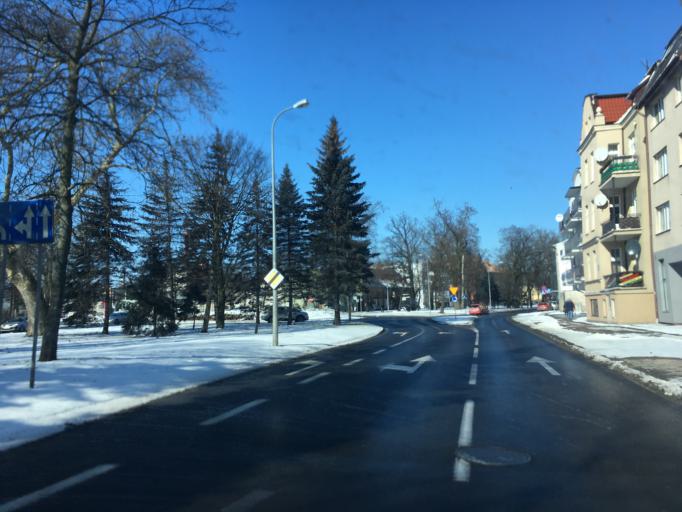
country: PL
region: Pomeranian Voivodeship
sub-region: Slupsk
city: Slupsk
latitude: 54.4699
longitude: 17.0286
